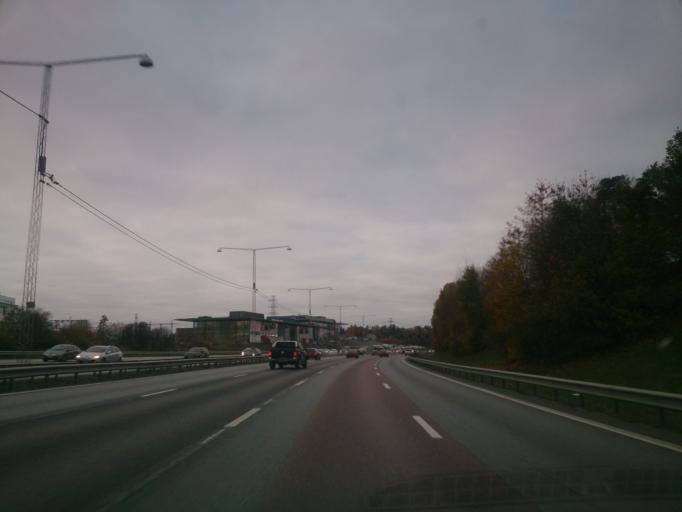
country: SE
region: Stockholm
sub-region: Stockholms Kommun
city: Kista
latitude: 59.4197
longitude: 17.9288
